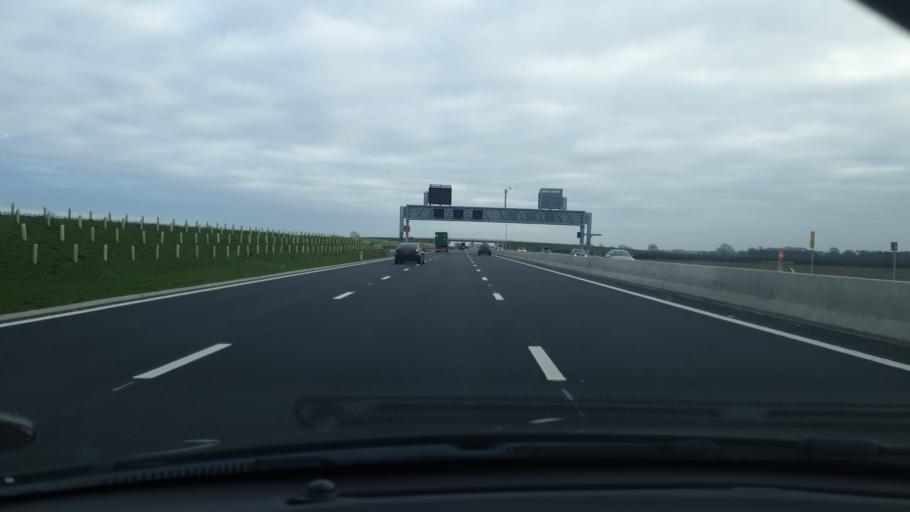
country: GB
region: England
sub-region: Cambridgeshire
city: Hemingford Grey
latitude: 52.2900
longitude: -0.0794
